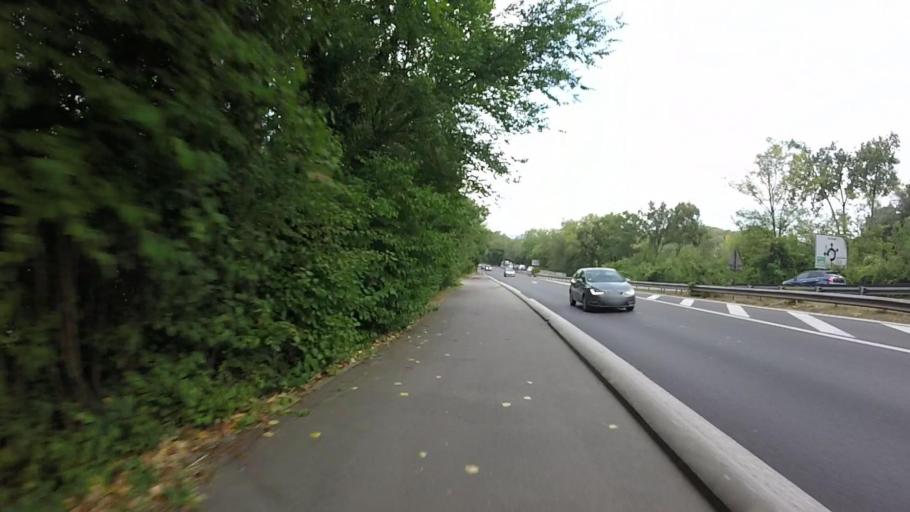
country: FR
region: Provence-Alpes-Cote d'Azur
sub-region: Departement des Alpes-Maritimes
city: Vallauris
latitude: 43.6147
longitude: 7.0426
